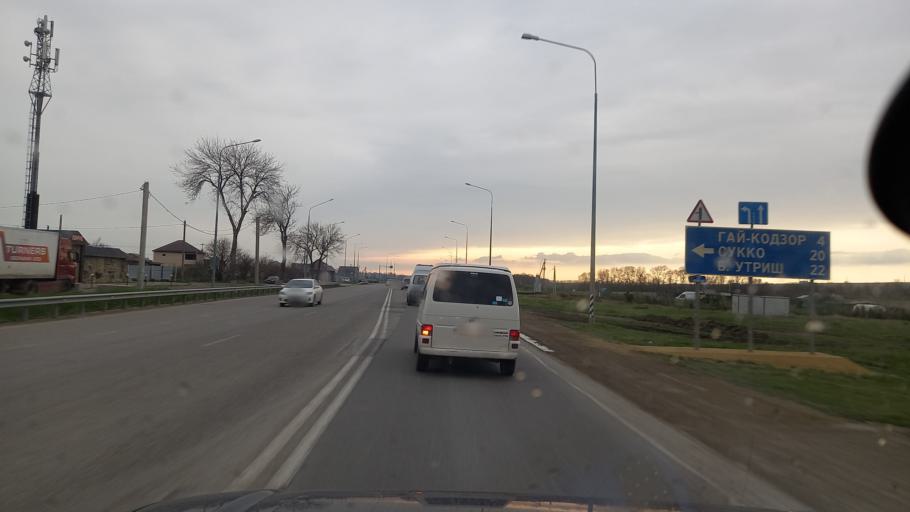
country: RU
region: Krasnodarskiy
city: Anapskaya
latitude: 44.8970
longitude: 37.4624
